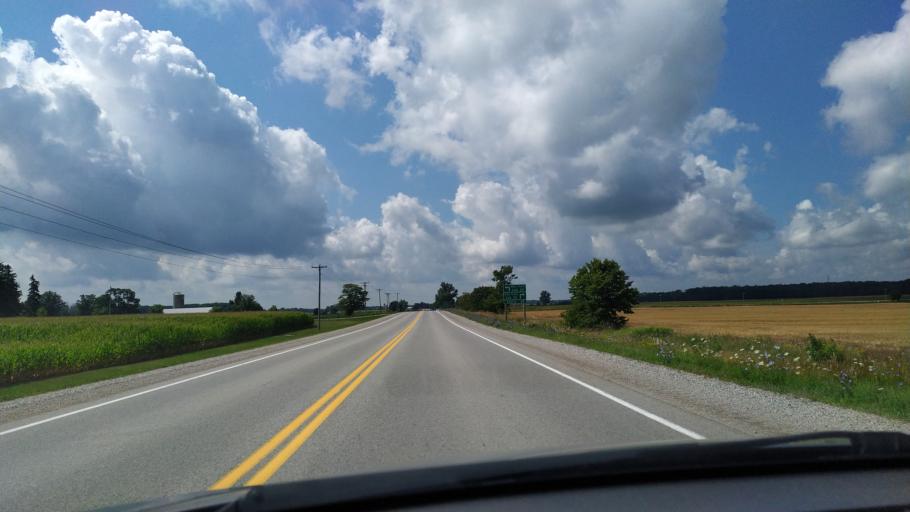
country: CA
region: Ontario
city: Huron East
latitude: 43.4079
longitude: -81.2492
